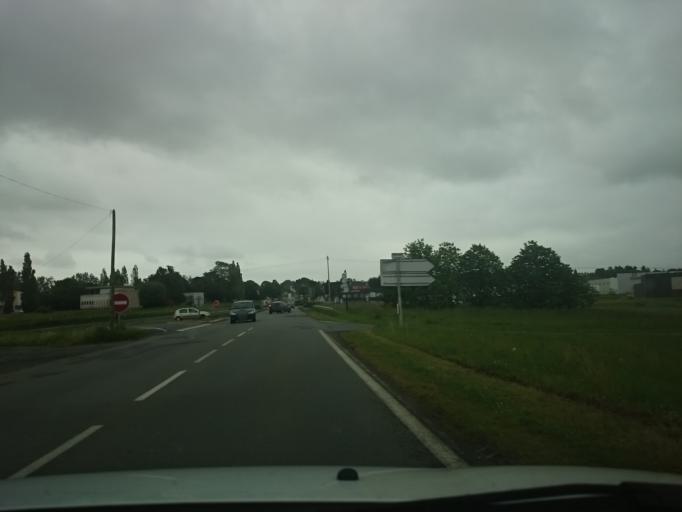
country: FR
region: Brittany
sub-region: Departement des Cotes-d'Armor
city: Guingamp
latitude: 48.5505
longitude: -3.1477
